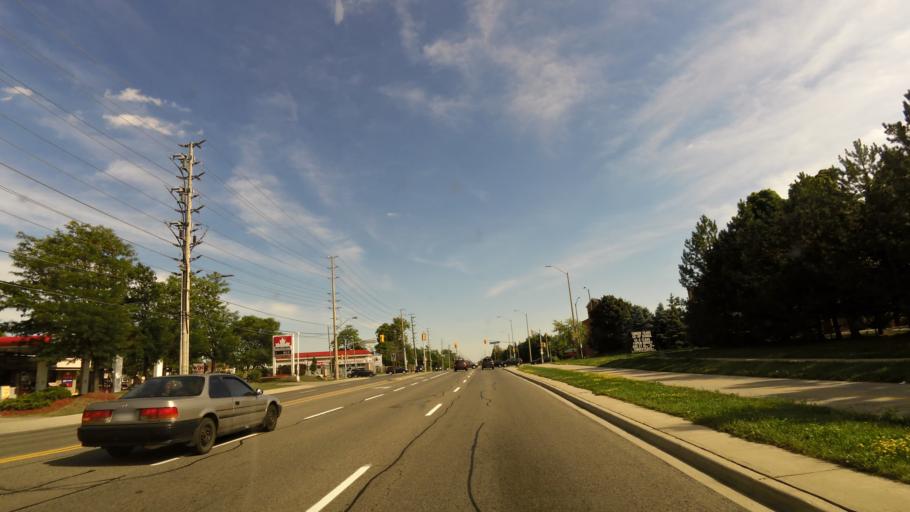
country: CA
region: Ontario
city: Mississauga
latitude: 43.5315
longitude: -79.6936
